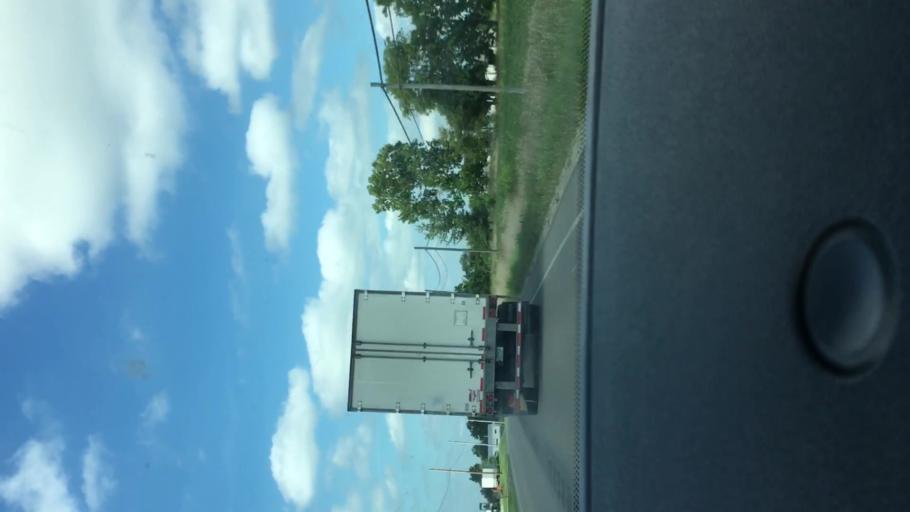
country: US
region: Indiana
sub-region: Jay County
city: Portland
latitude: 40.4777
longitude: -84.9794
